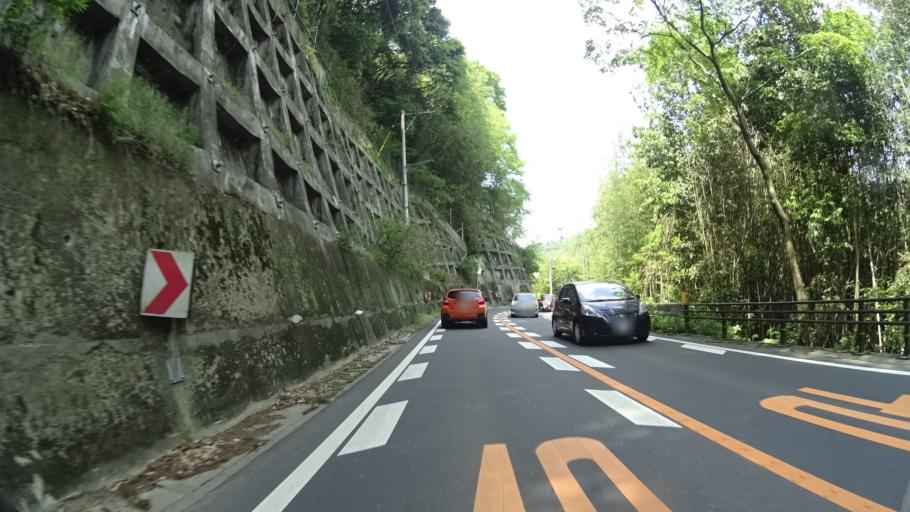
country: JP
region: Ehime
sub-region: Shikoku-chuo Shi
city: Matsuyama
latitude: 33.8888
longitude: 132.8356
